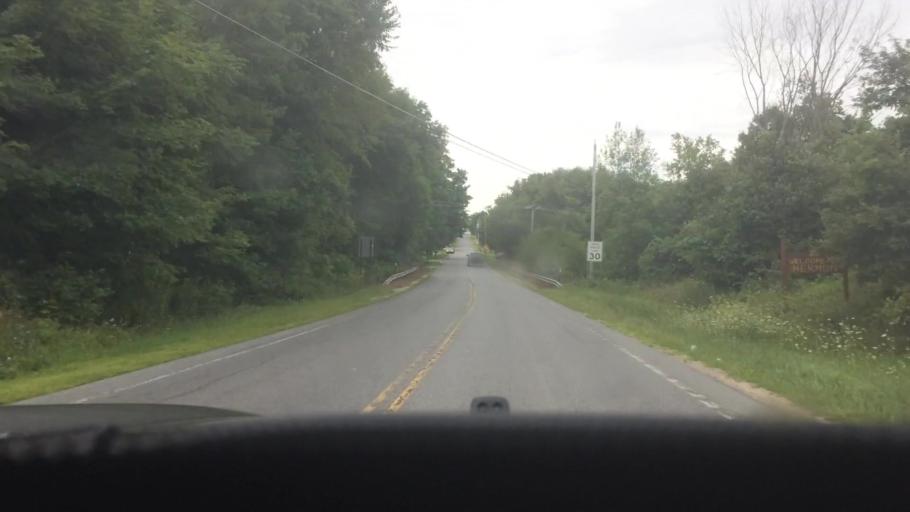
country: US
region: New York
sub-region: St. Lawrence County
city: Canton
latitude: 44.4726
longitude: -75.2290
